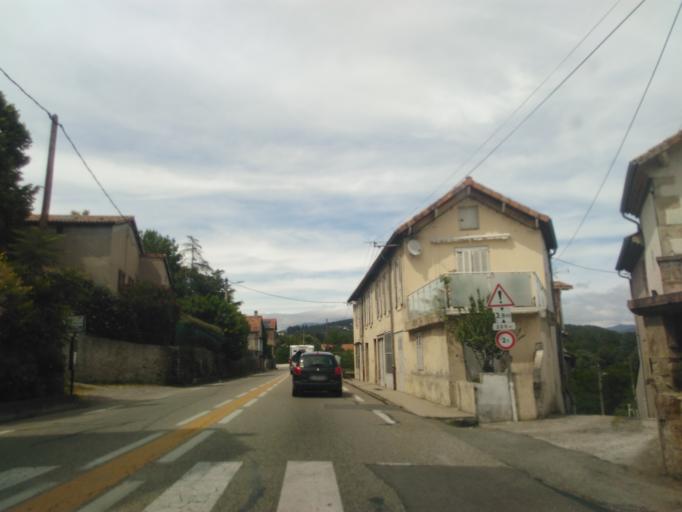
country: FR
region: Rhone-Alpes
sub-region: Departement de l'Ardeche
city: Aubenas
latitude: 44.6335
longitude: 4.3797
